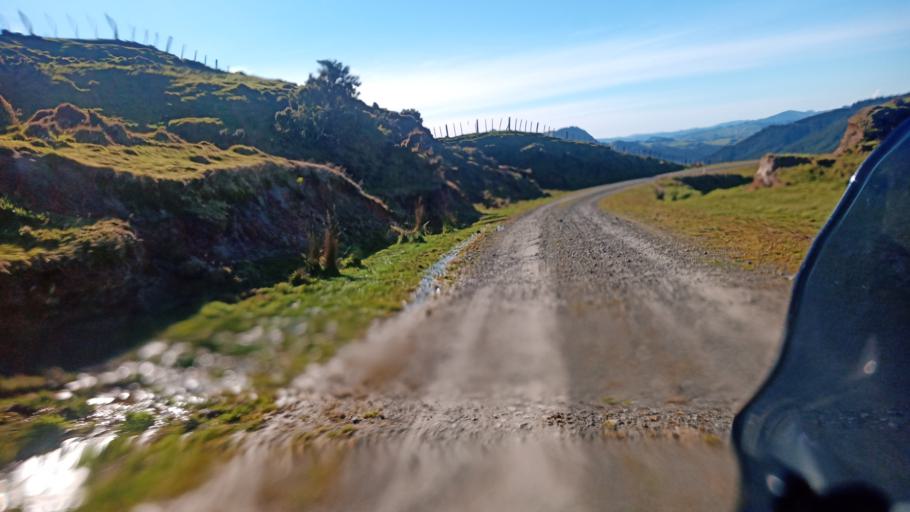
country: NZ
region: Gisborne
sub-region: Gisborne District
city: Gisborne
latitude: -38.1494
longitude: 177.8781
